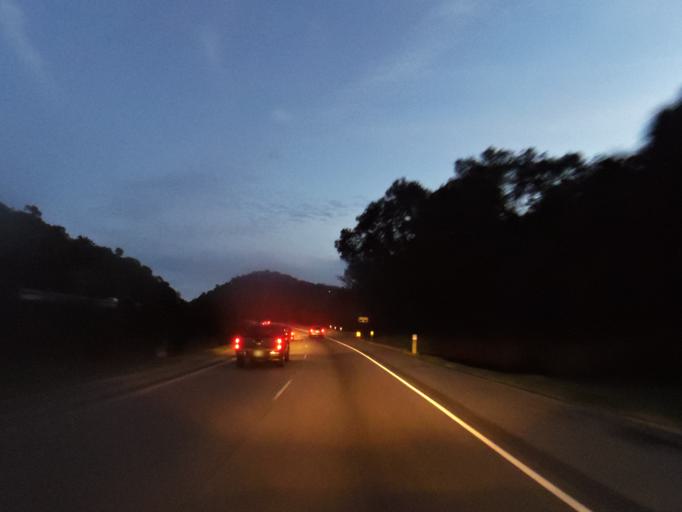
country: US
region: California
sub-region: San Luis Obispo County
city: Santa Margarita
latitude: 35.3554
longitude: -120.6367
